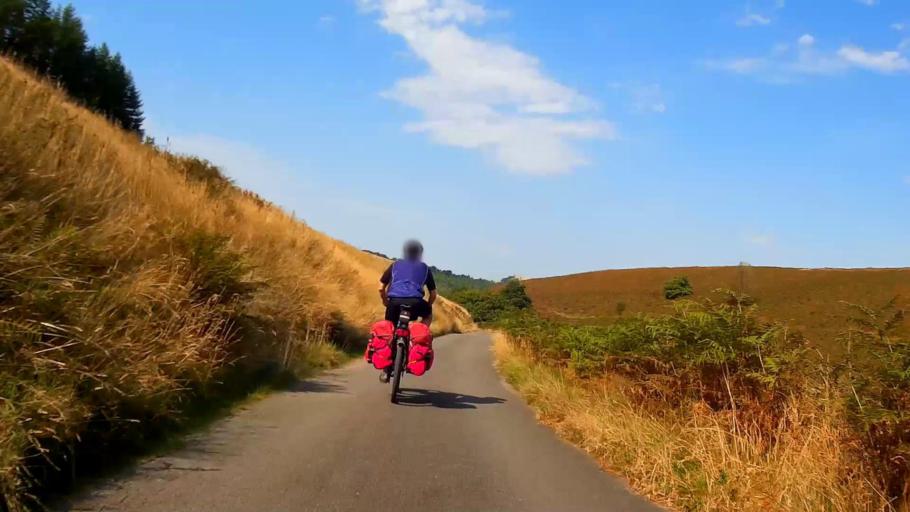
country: GB
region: England
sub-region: Derbyshire
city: Buxton
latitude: 53.2544
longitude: -1.9798
